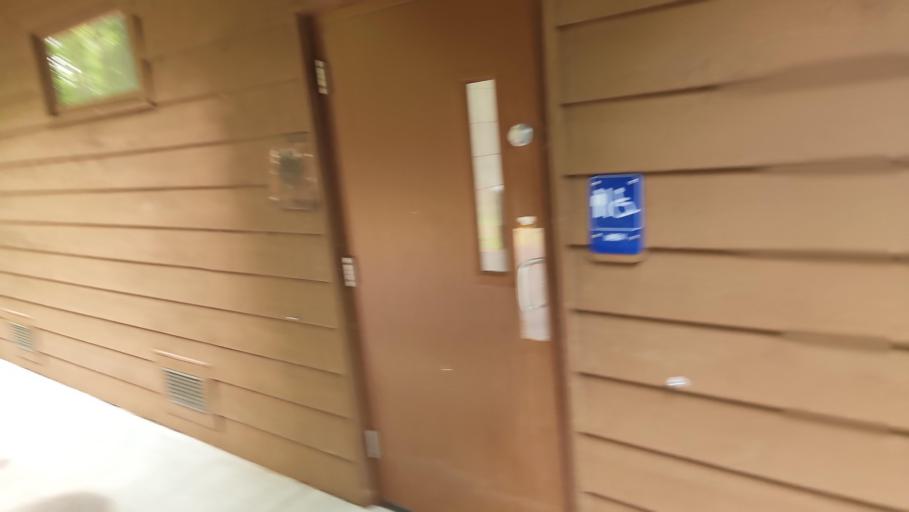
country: CA
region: Ontario
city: Brockville
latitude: 44.5587
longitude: -75.6887
